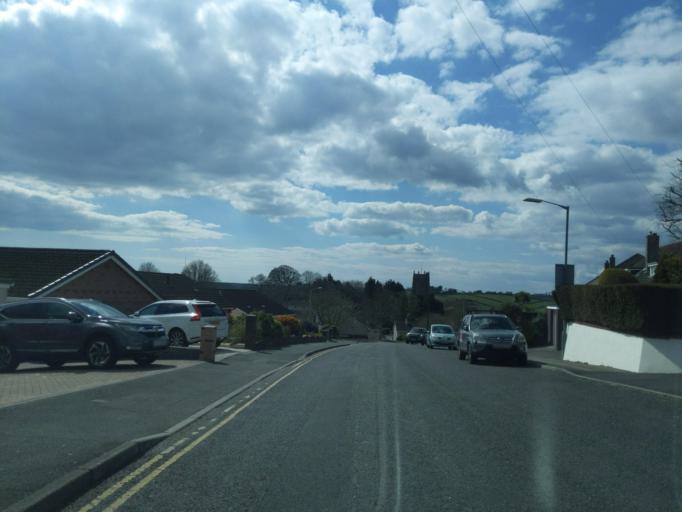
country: GB
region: England
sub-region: Cornwall
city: Saltash
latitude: 50.4046
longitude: -4.2254
